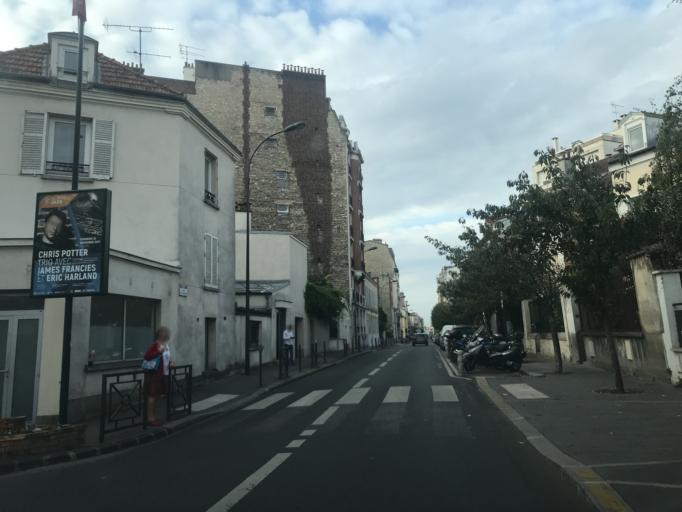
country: FR
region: Ile-de-France
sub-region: Departement du Val-de-Marne
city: Vincennes
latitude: 48.8526
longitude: 2.4386
